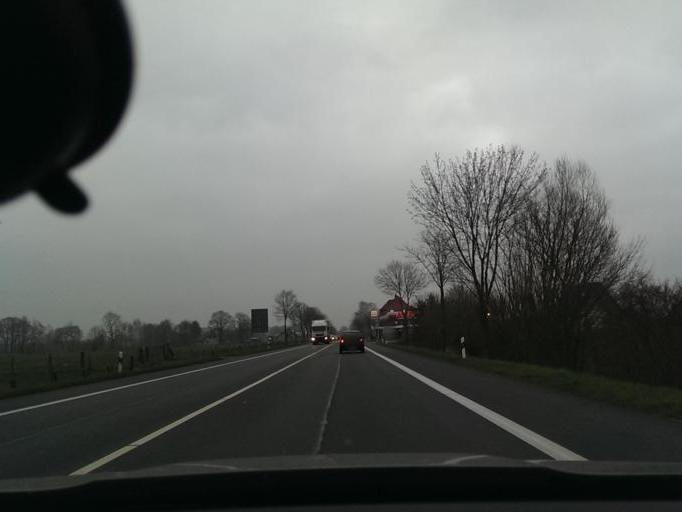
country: DE
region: North Rhine-Westphalia
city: Rietberg
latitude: 51.7821
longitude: 8.4728
